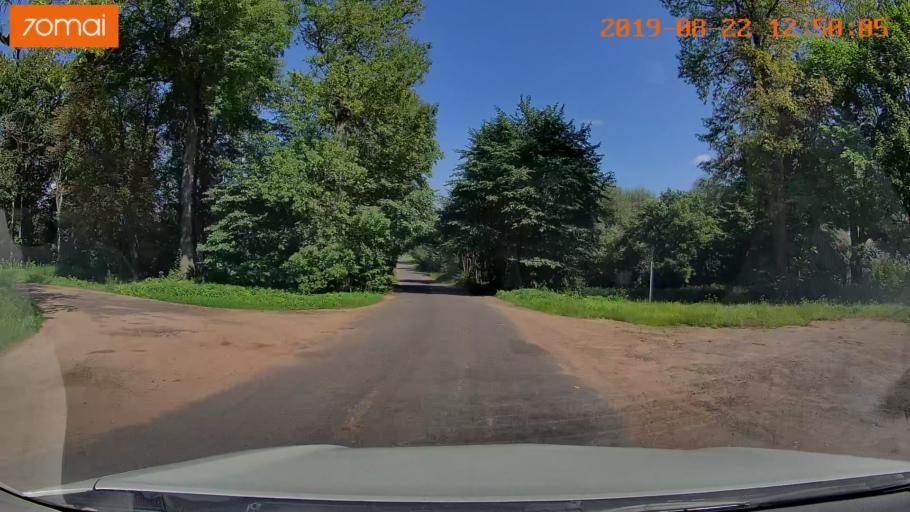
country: BY
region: Minsk
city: Prawdzinski
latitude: 53.4582
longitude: 27.6407
